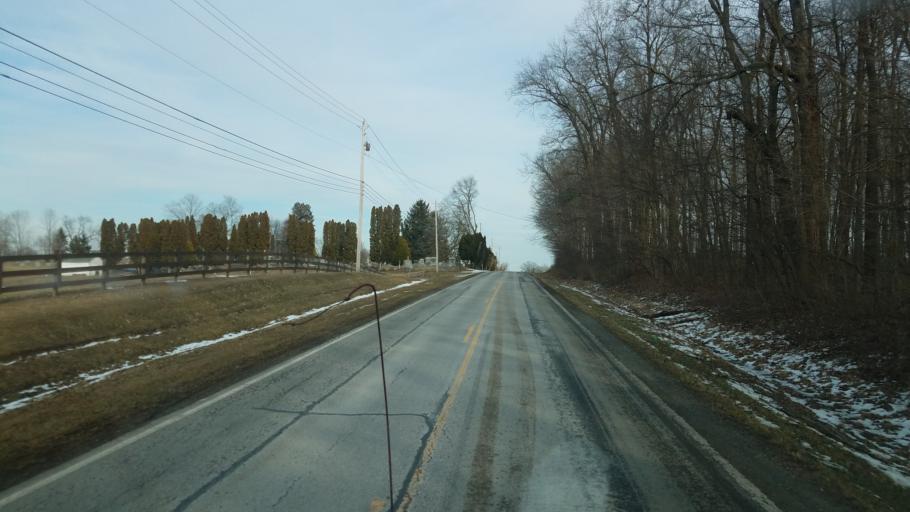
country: US
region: Ohio
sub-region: Marion County
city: Prospect
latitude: 40.5278
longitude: -83.2026
